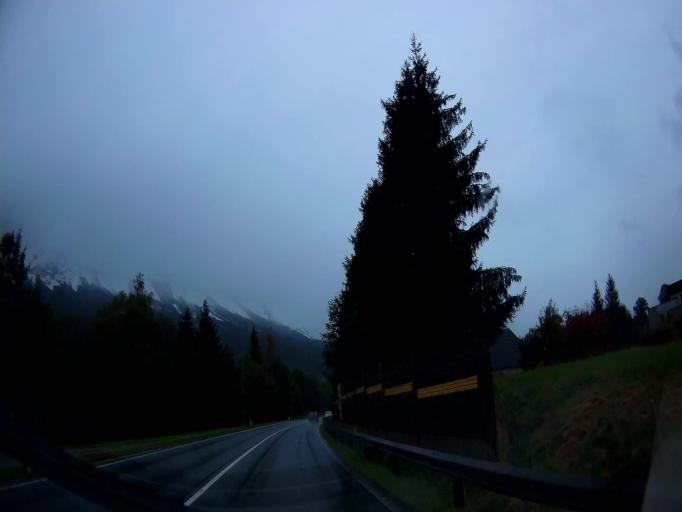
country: AT
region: Styria
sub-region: Politischer Bezirk Liezen
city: Sankt Martin am Grimming
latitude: 47.4813
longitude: 13.9644
